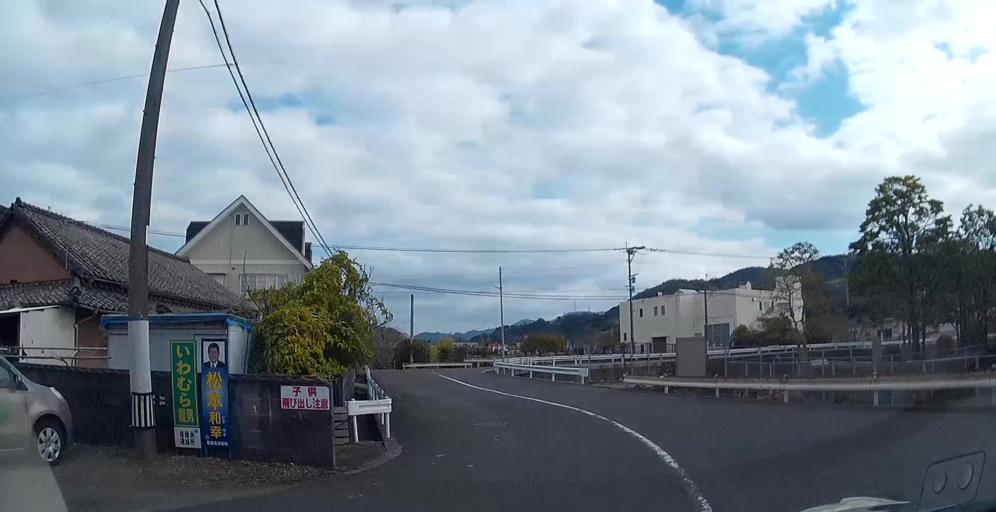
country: JP
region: Kumamoto
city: Minamata
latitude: 32.2029
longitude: 130.3886
